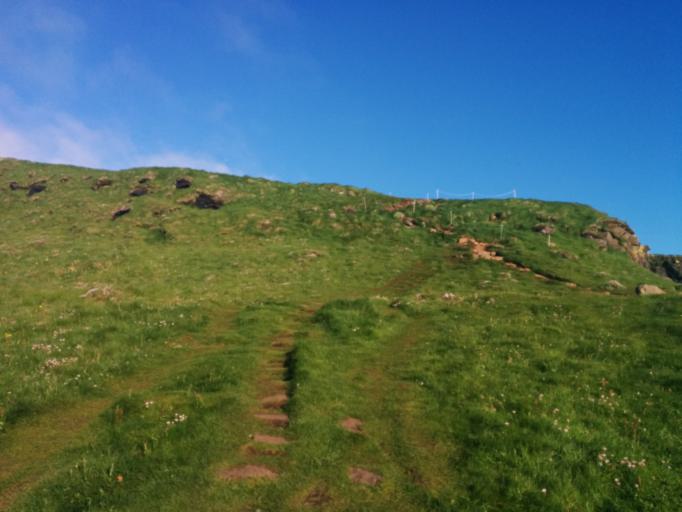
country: IS
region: West
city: Olafsvik
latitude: 65.5008
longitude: -24.5275
